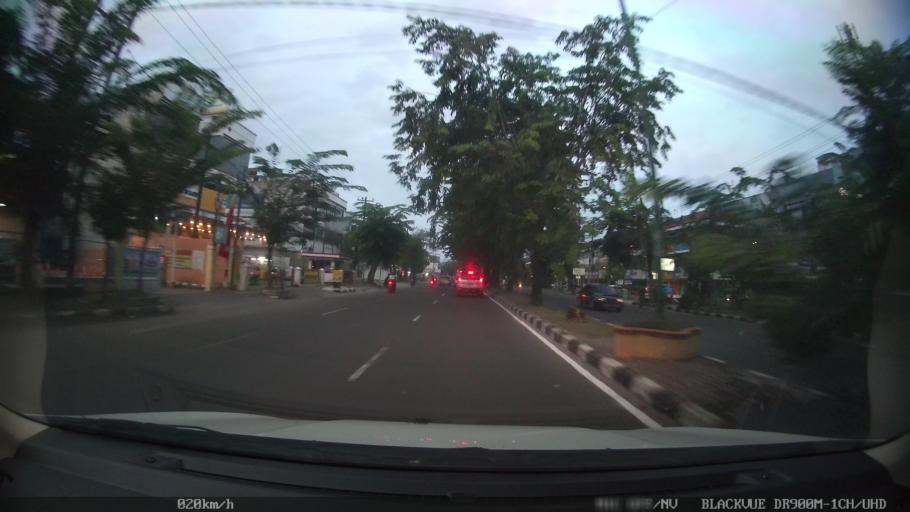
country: ID
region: North Sumatra
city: Medan
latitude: 3.5910
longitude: 98.6403
